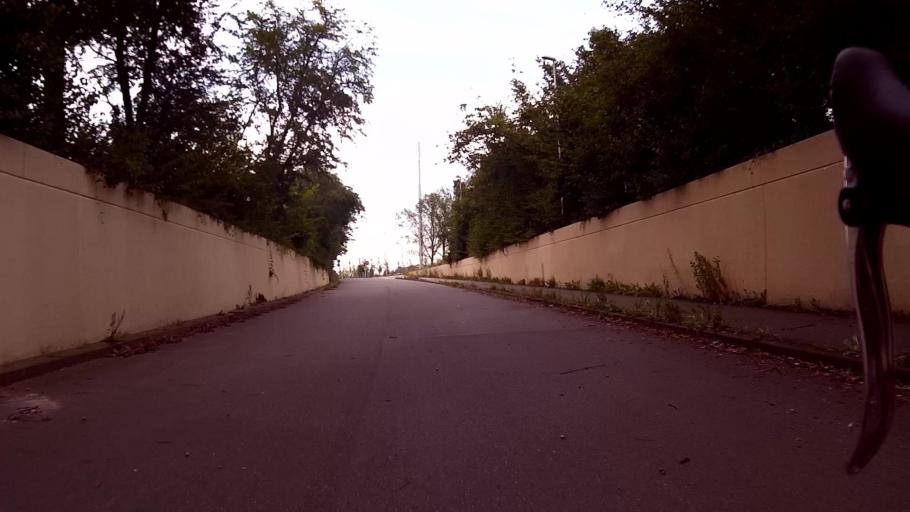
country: NL
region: Utrecht
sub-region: Gemeente Utrecht
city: Utrecht
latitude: 52.1033
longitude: 5.1502
